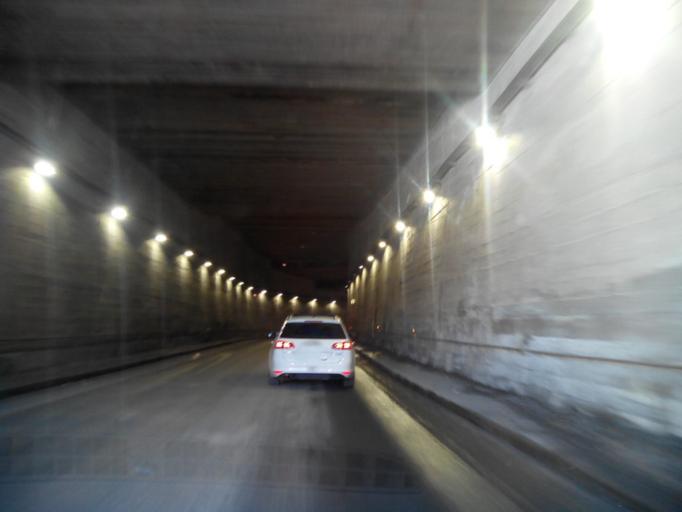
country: ES
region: Catalonia
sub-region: Provincia de Girona
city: Alp
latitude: 42.3397
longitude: 1.9438
